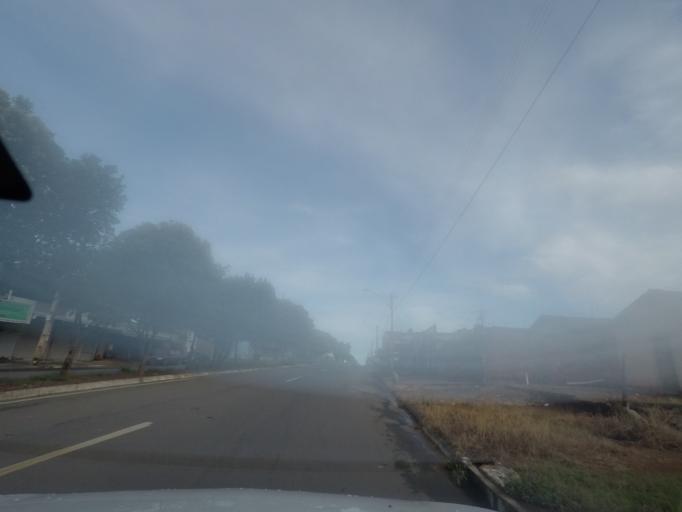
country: BR
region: Goias
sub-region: Aparecida De Goiania
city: Aparecida de Goiania
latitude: -16.7817
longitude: -49.3844
